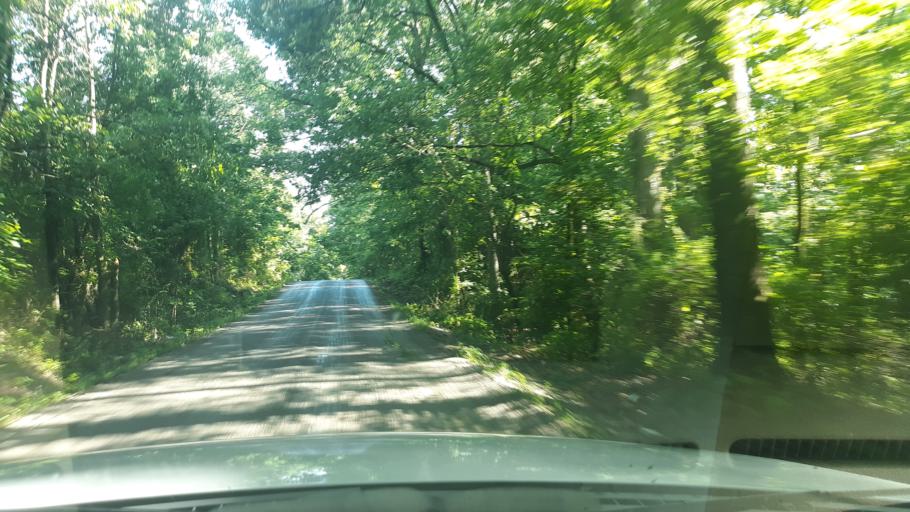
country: US
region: Illinois
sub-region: Saline County
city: Harrisburg
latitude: 37.8446
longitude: -88.5814
